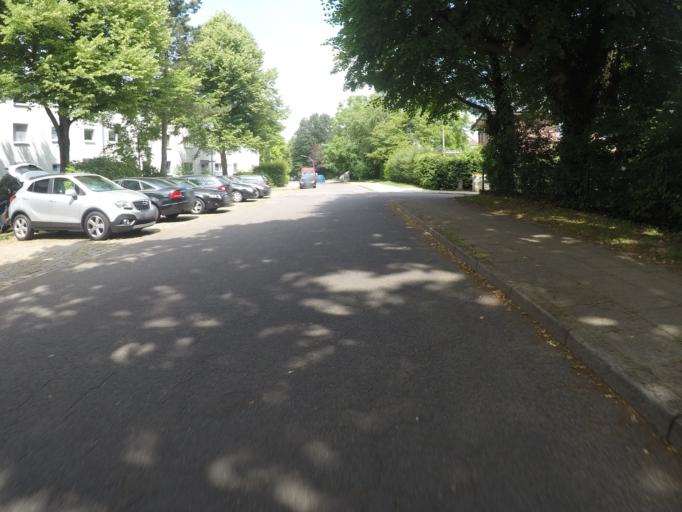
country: DE
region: Hamburg
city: Eidelstedt
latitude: 53.5689
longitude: 9.8705
